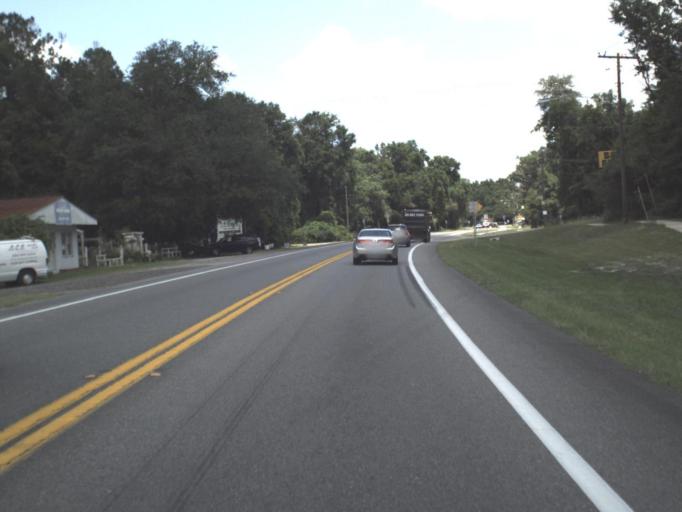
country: US
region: Florida
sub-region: Alachua County
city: High Springs
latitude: 29.9181
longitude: -82.7087
